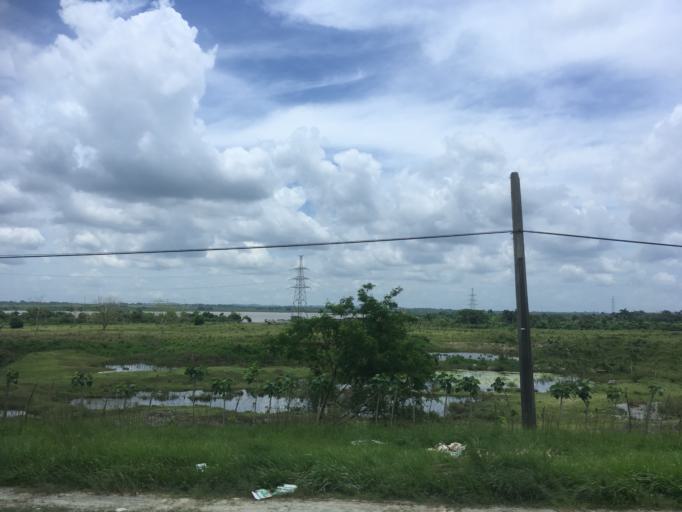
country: CU
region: Villa Clara
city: Esperanza
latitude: 22.4314
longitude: -80.0554
